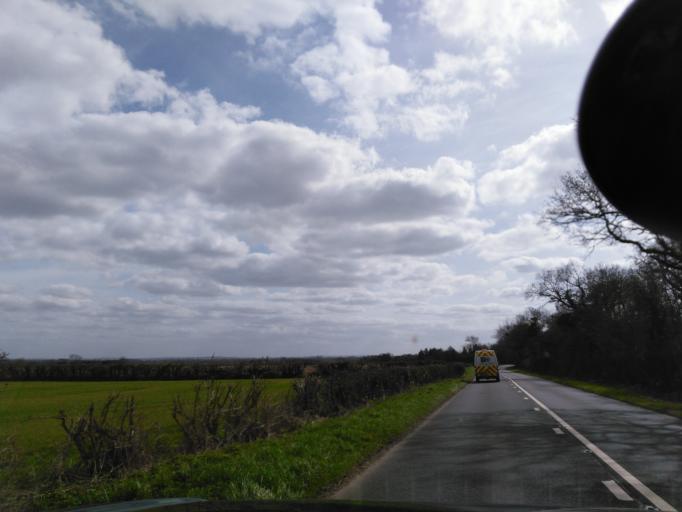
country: GB
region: England
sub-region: Wiltshire
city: Hankerton
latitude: 51.6438
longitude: -2.0600
